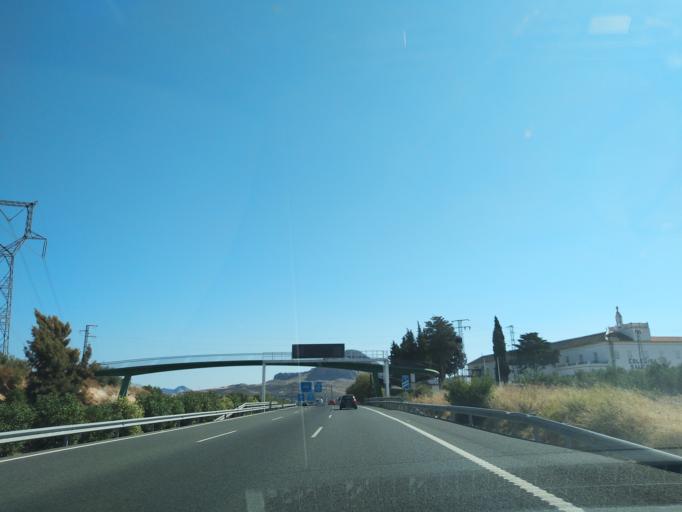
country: ES
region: Andalusia
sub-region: Provincia de Malaga
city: Antequera
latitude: 37.0701
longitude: -4.5397
